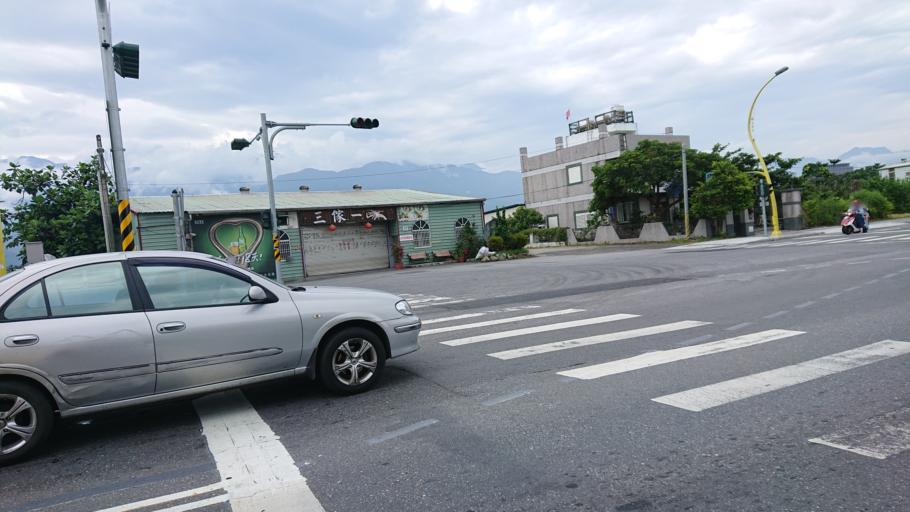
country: TW
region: Taiwan
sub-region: Hualien
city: Hualian
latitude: 23.9648
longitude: 121.6070
